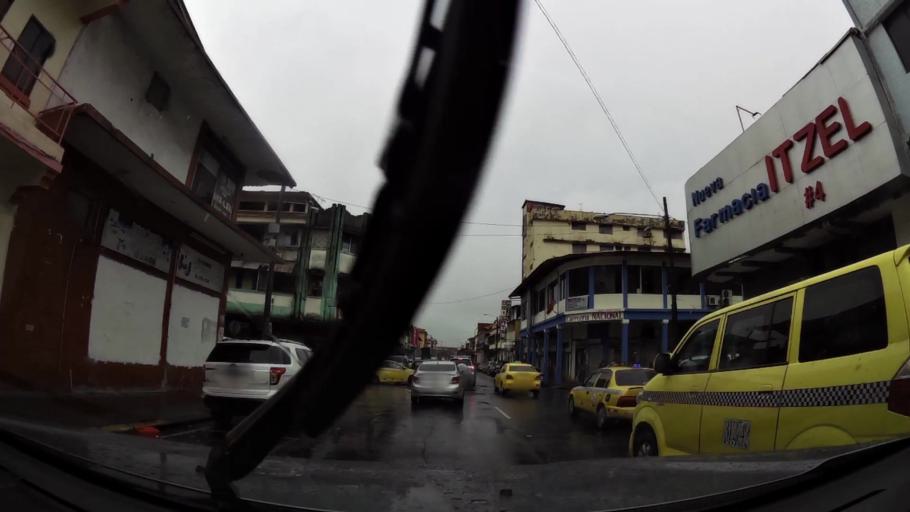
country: PA
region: Colon
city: Colon
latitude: 9.3558
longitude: -79.9023
